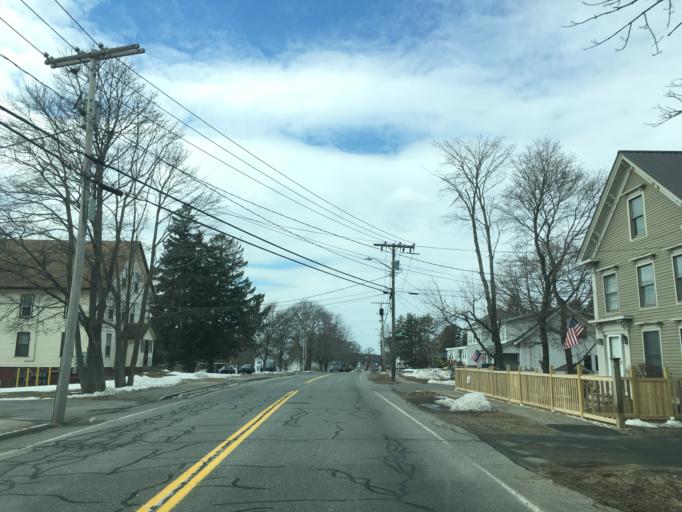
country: US
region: New Hampshire
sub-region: Rockingham County
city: Hampton
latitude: 42.9396
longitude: -70.8305
